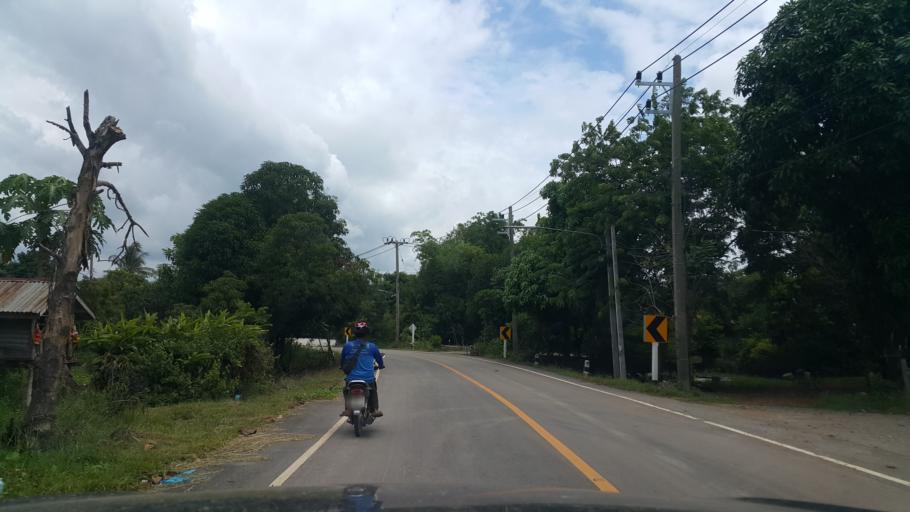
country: TH
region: Sukhothai
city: Kong Krailat
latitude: 16.9326
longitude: 99.9416
